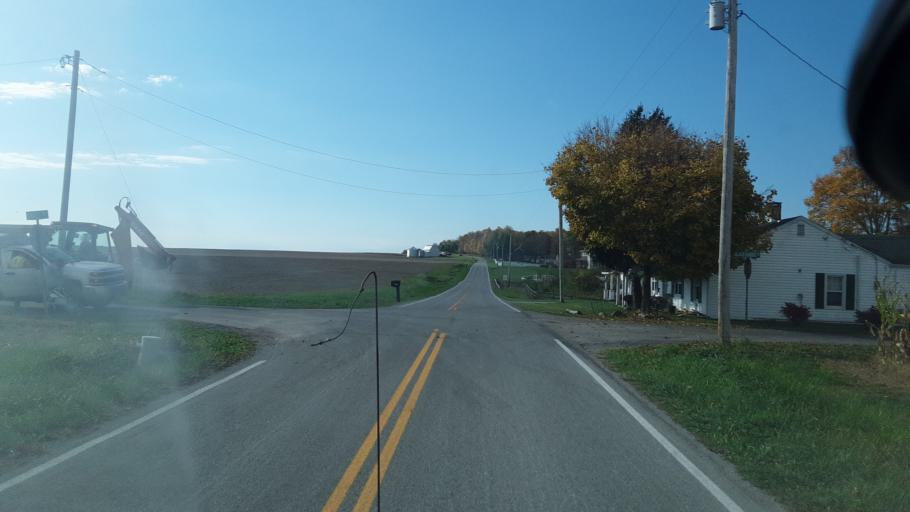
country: US
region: Ohio
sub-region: Highland County
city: Leesburg
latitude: 39.2842
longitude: -83.5352
